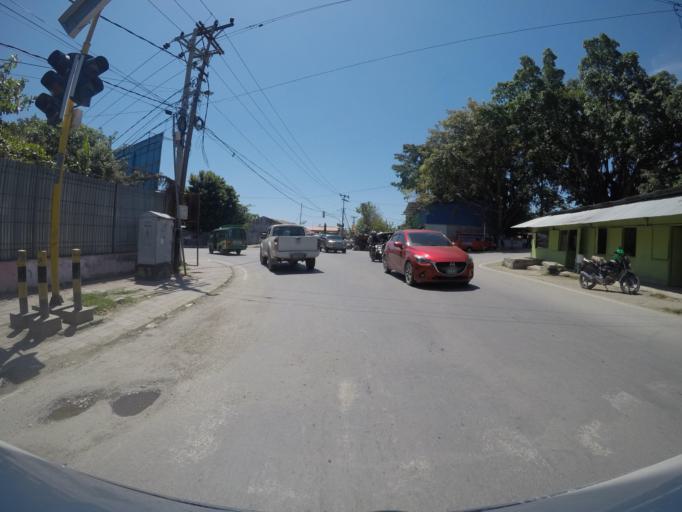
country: TL
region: Dili
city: Dili
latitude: -8.5549
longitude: 125.5914
